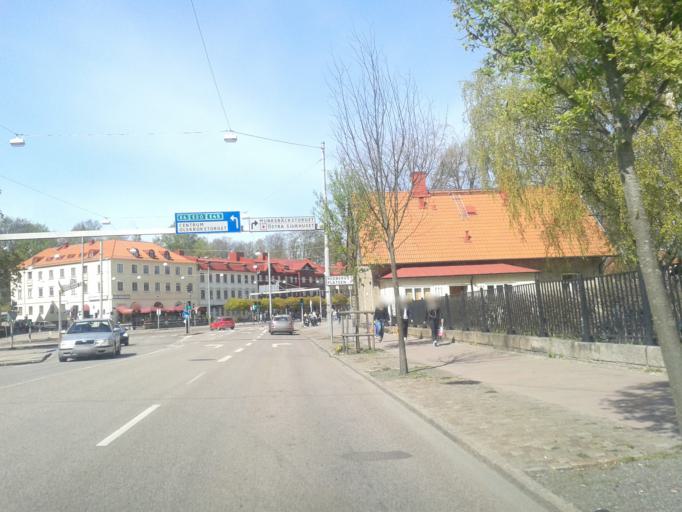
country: SE
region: Vaestra Goetaland
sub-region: Goteborg
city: Goeteborg
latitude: 57.7148
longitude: 12.0048
